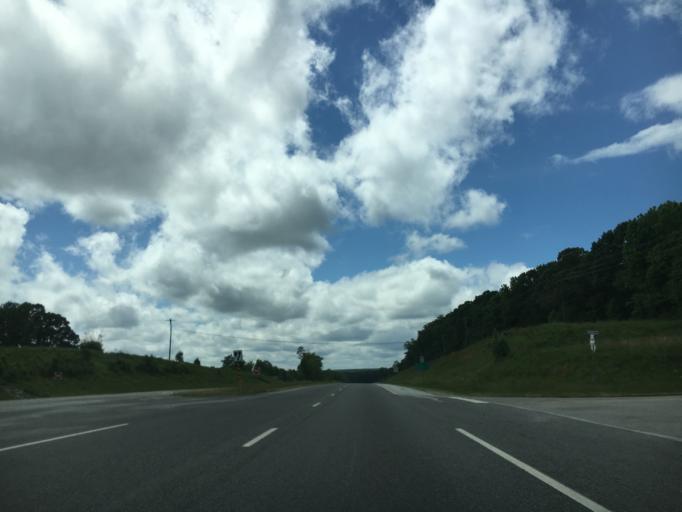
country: US
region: Virginia
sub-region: Mecklenburg County
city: Boydton
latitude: 36.6717
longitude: -78.2882
